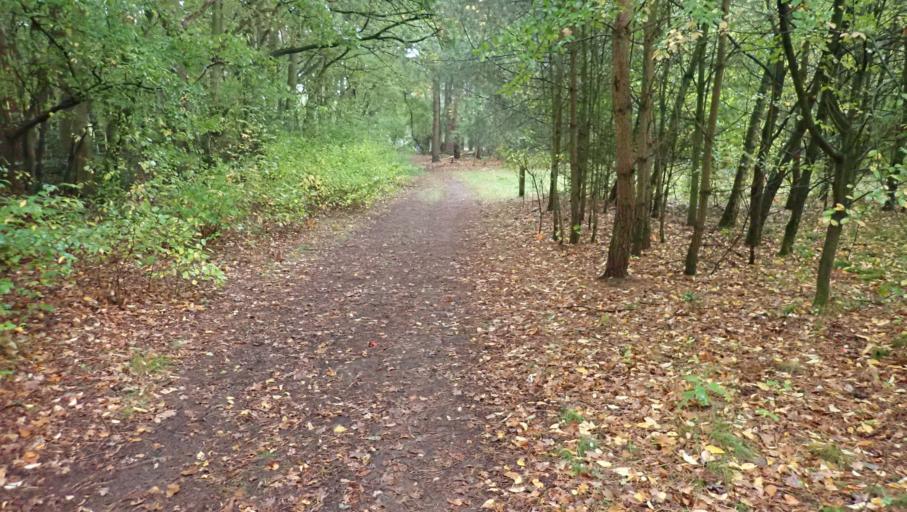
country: BE
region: Flanders
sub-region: Provincie Antwerpen
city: Nijlen
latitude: 51.1512
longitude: 4.6834
